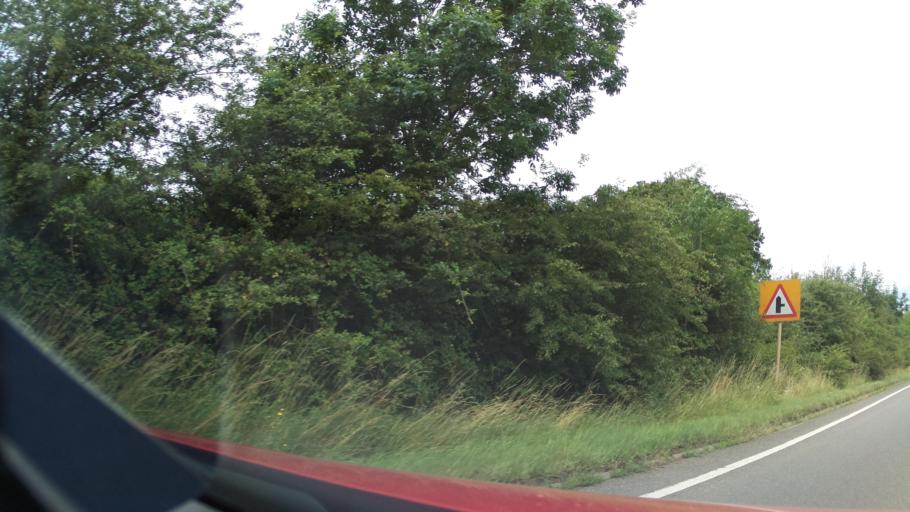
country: GB
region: England
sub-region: Northamptonshire
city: Corby
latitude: 52.4742
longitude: -0.7402
